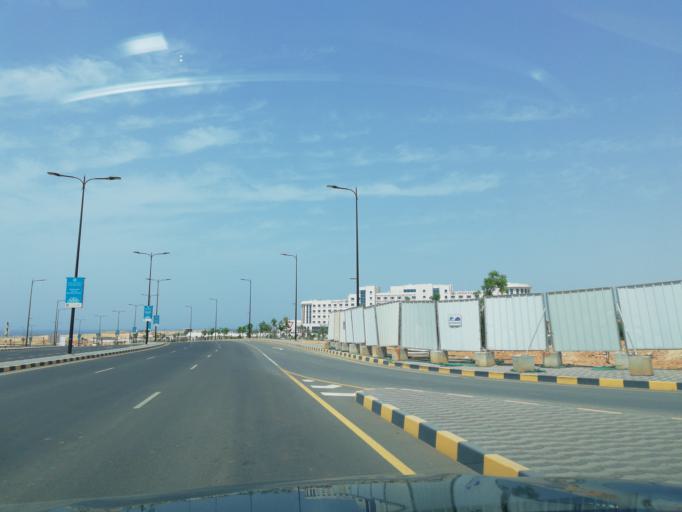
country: OM
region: Muhafazat Masqat
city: Bawshar
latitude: 23.5703
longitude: 58.3245
